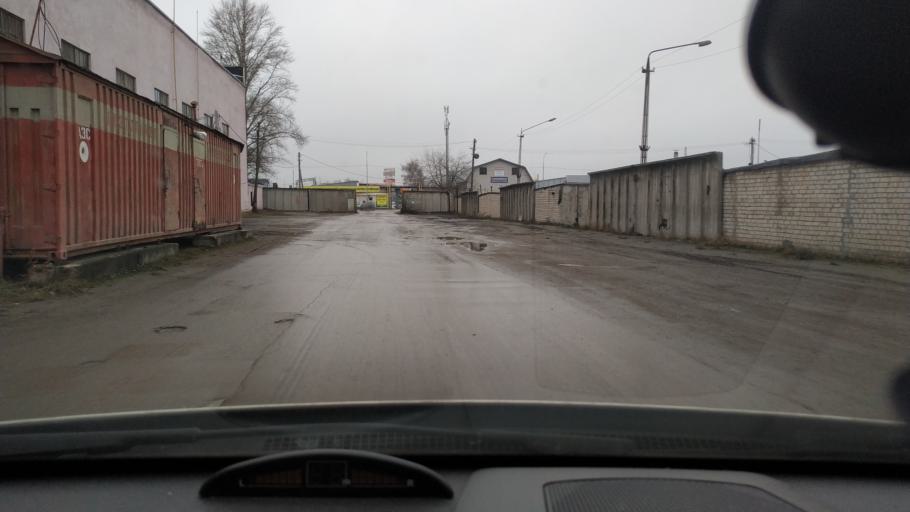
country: RU
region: Rjazan
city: Ryazan'
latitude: 54.6560
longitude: 39.6405
